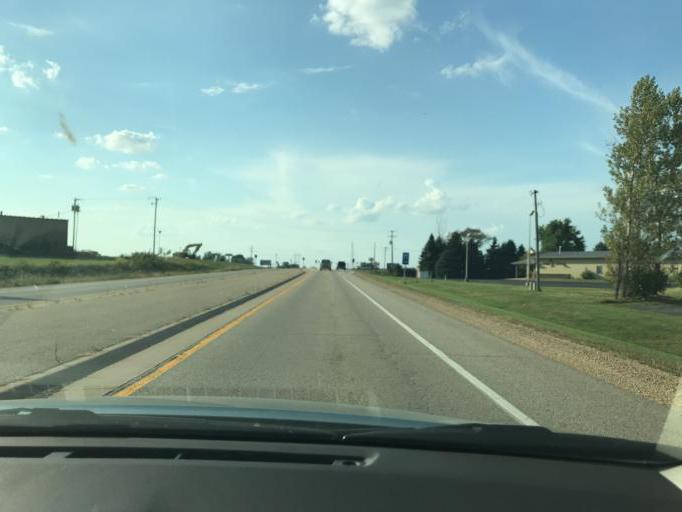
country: US
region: Wisconsin
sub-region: Grant County
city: Platteville
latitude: 42.7153
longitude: -90.4592
